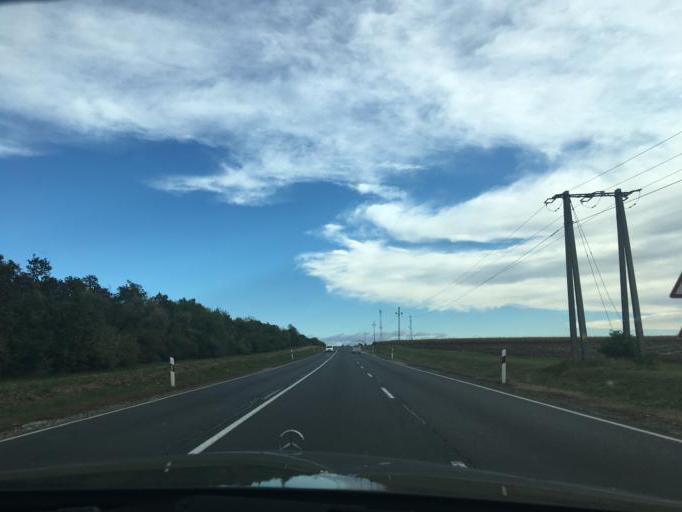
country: HU
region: Borsod-Abauj-Zemplen
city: Arnot
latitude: 48.1471
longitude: 20.8914
